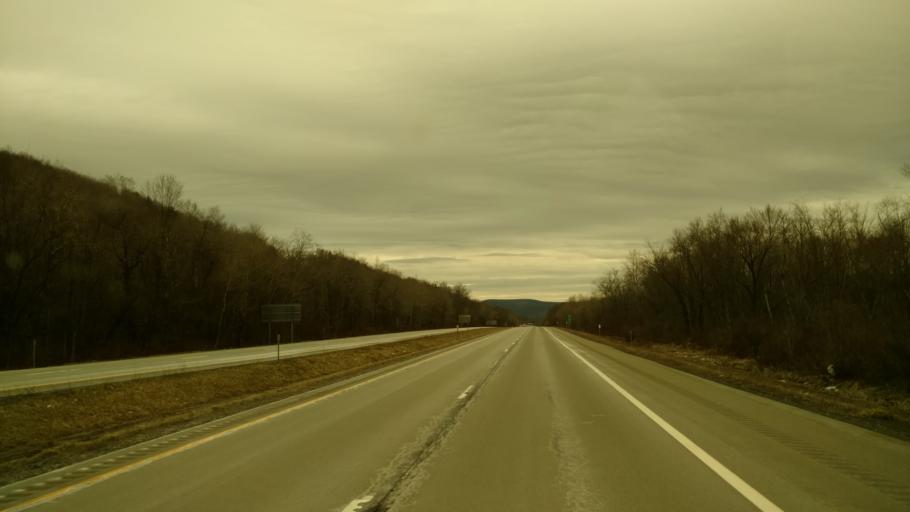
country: US
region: New York
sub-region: Cattaraugus County
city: Salamanca
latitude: 42.1474
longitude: -78.7670
